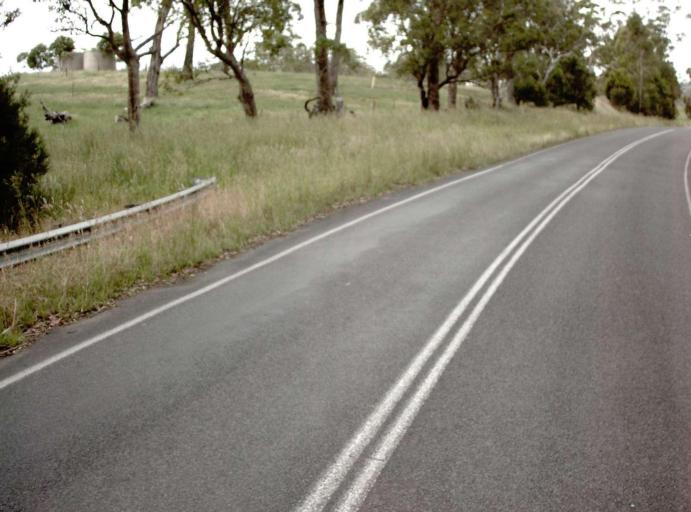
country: AU
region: Victoria
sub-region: Latrobe
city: Moe
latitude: -38.1370
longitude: 146.2600
